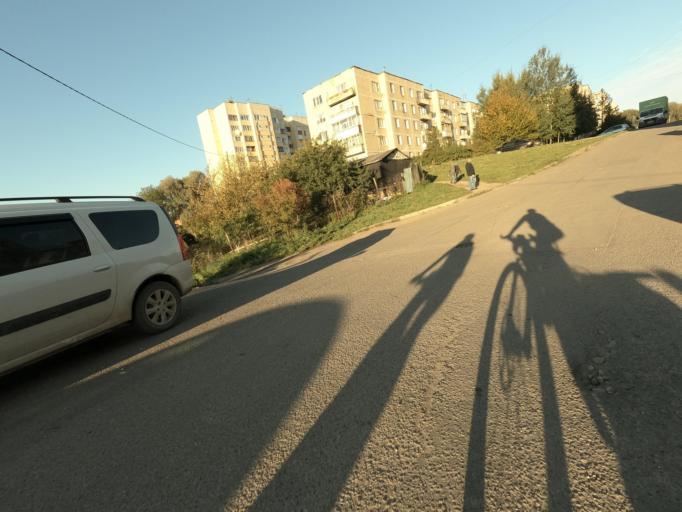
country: RU
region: Leningrad
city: Nikol'skoye
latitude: 59.7083
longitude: 30.7756
